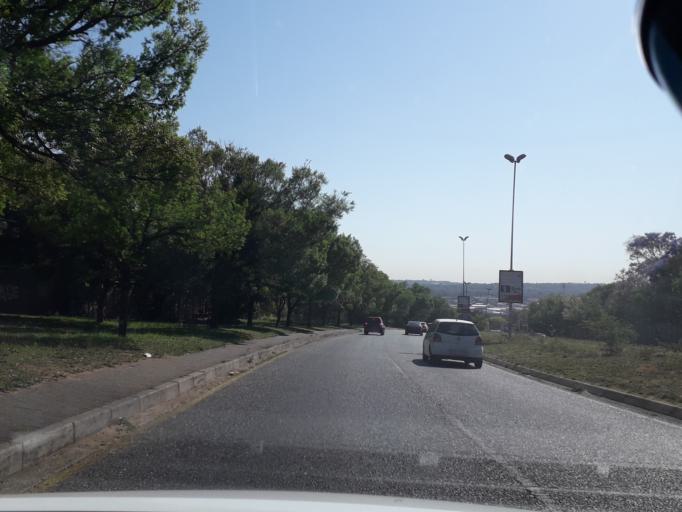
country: ZA
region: Gauteng
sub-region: City of Johannesburg Metropolitan Municipality
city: Roodepoort
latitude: -26.0931
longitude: 27.9562
